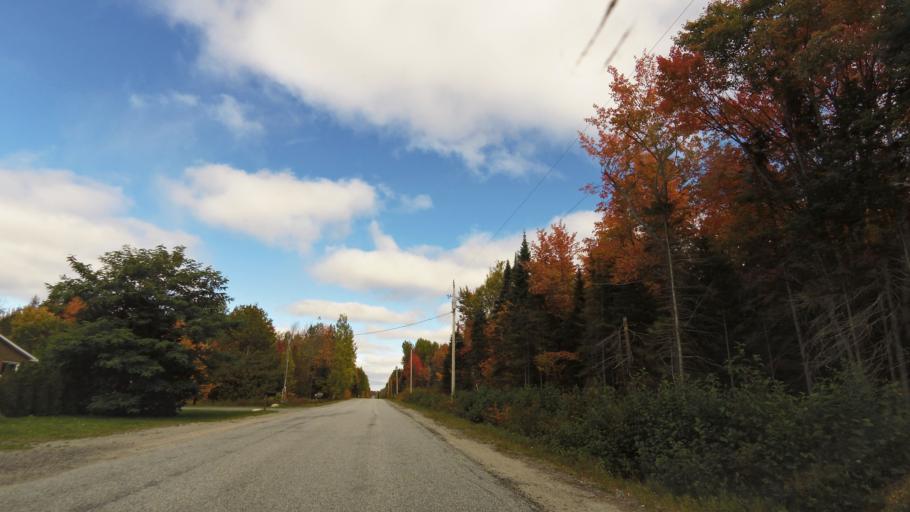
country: CA
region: Ontario
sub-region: Nipissing District
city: North Bay
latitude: 46.3541
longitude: -79.4871
